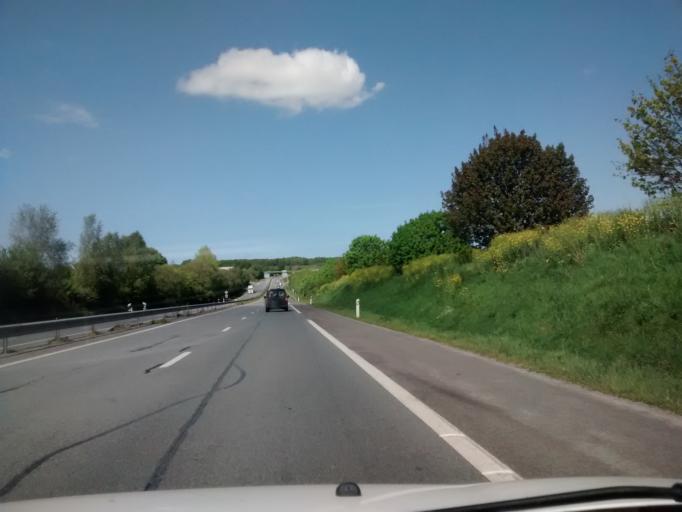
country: FR
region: Brittany
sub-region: Departement des Cotes-d'Armor
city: Saint-Samson-sur-Rance
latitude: 48.5138
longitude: -2.0389
